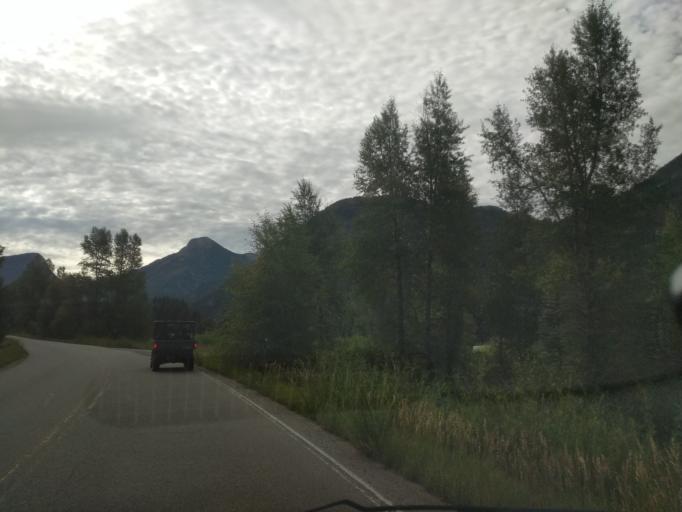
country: US
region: Colorado
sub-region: Gunnison County
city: Crested Butte
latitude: 39.0762
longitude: -107.2220
